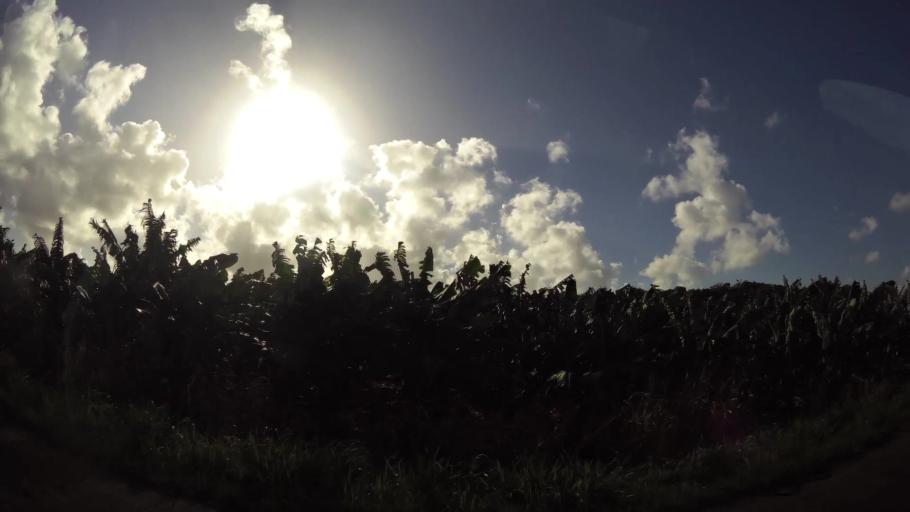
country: MQ
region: Martinique
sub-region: Martinique
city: Ducos
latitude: 14.5956
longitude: -60.9802
